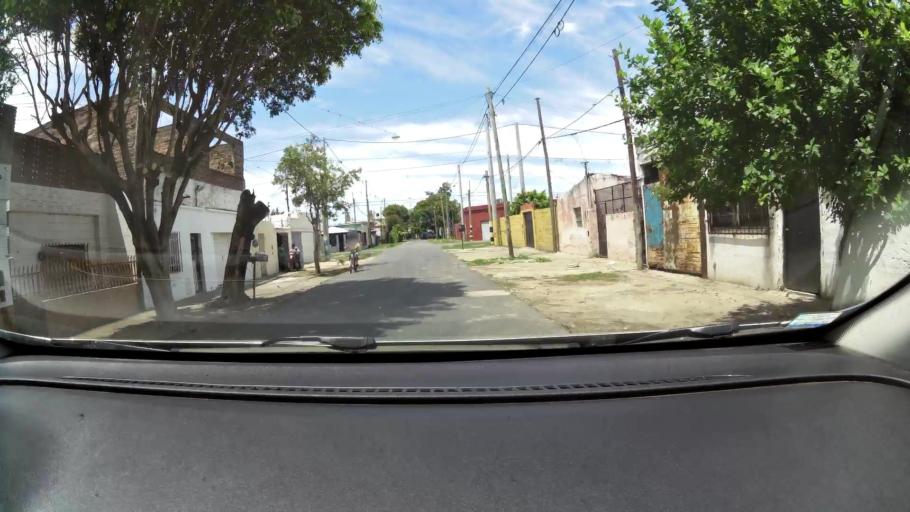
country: AR
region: Santa Fe
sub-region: Departamento de Rosario
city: Rosario
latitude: -32.9852
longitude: -60.6269
